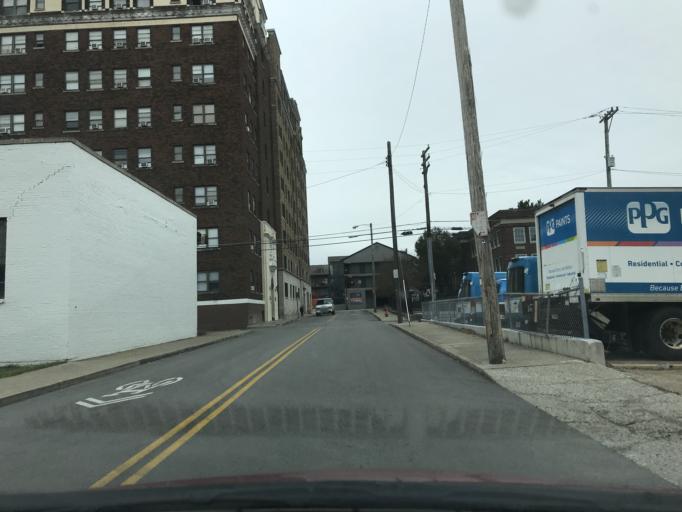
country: US
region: Kentucky
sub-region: Jefferson County
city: Louisville
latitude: 38.2440
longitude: -85.7567
